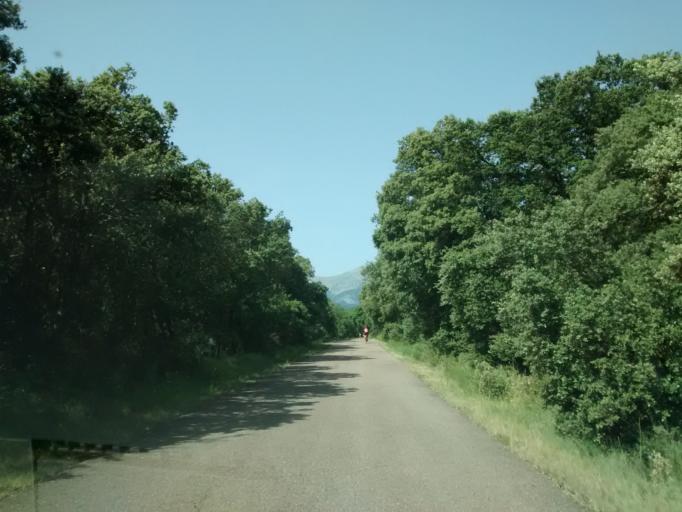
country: ES
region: Aragon
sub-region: Provincia de Zaragoza
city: Trasmoz
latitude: 41.8047
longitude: -1.7268
